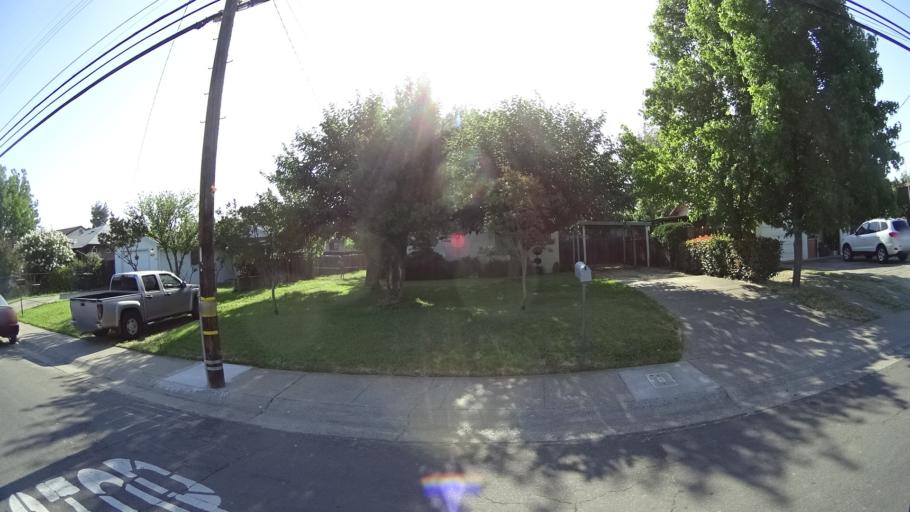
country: US
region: California
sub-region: Sacramento County
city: Florin
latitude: 38.5383
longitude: -121.4191
